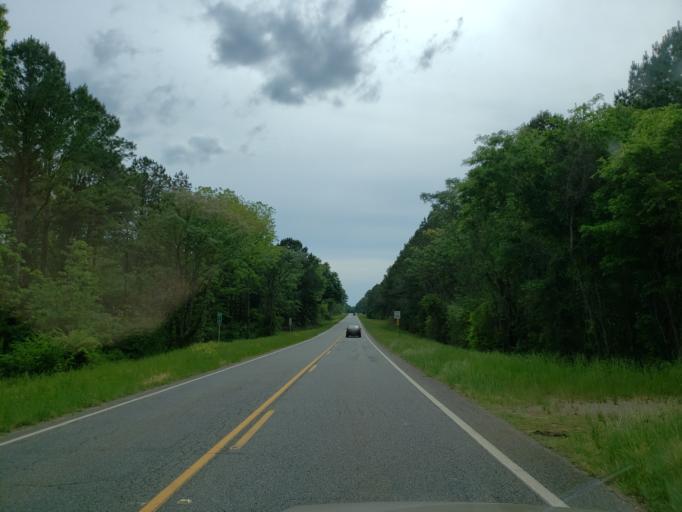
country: US
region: Georgia
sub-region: Macon County
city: Marshallville
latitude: 32.4185
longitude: -83.8495
